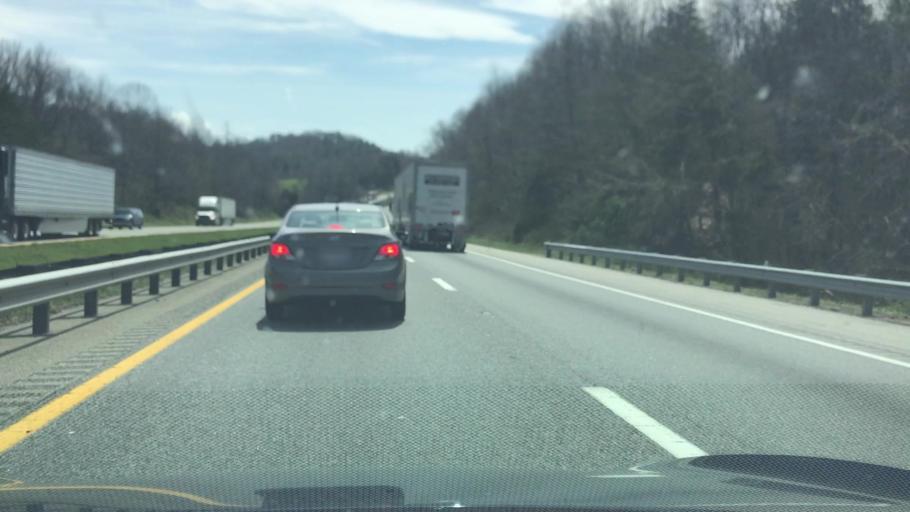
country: US
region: Virginia
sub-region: Pulaski County
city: Dublin
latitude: 37.0494
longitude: -80.7146
